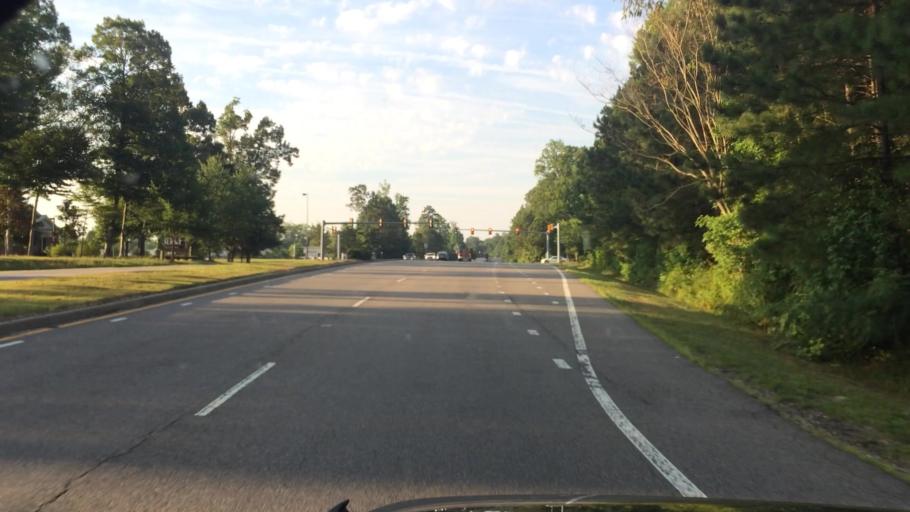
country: US
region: Virginia
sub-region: James City County
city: Williamsburg
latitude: 37.3406
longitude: -76.7389
